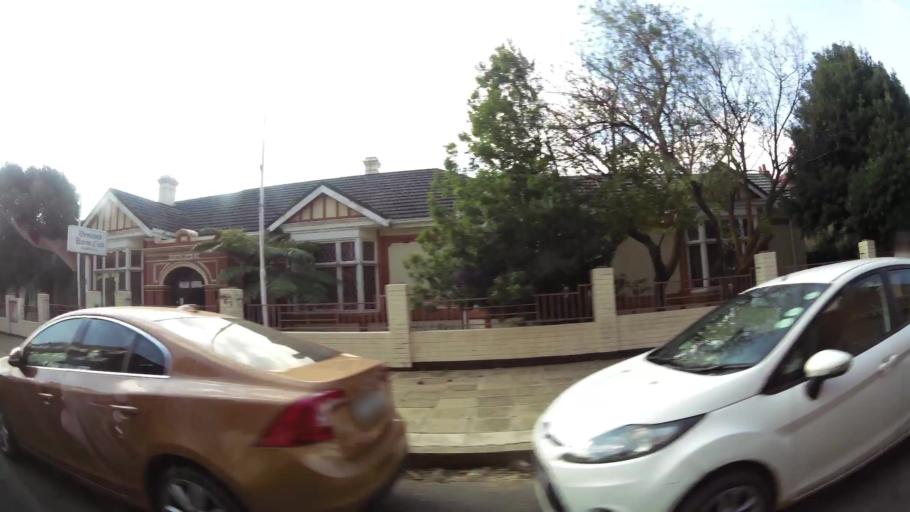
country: ZA
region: Gauteng
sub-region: West Rand District Municipality
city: Krugersdorp
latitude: -26.1037
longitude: 27.7759
